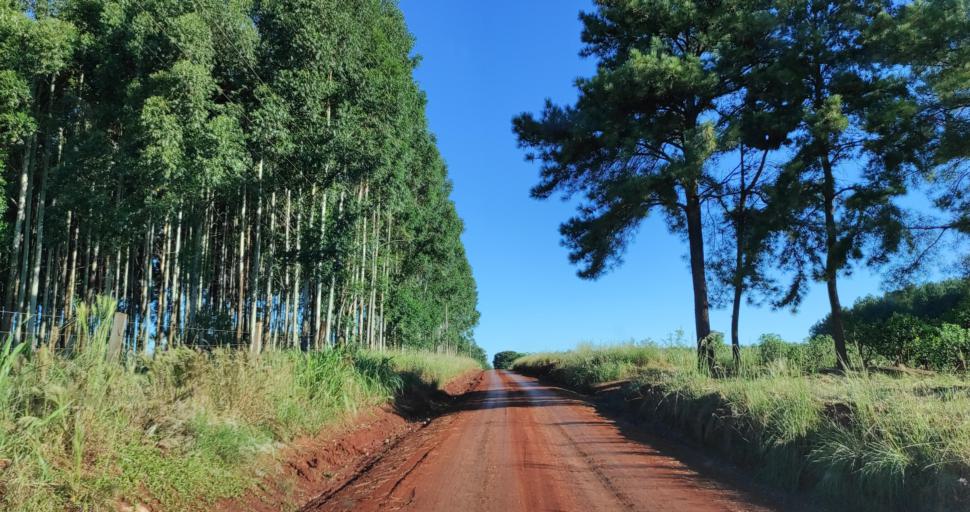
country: AR
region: Misiones
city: Puerto Rico
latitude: -26.8570
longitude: -55.0143
